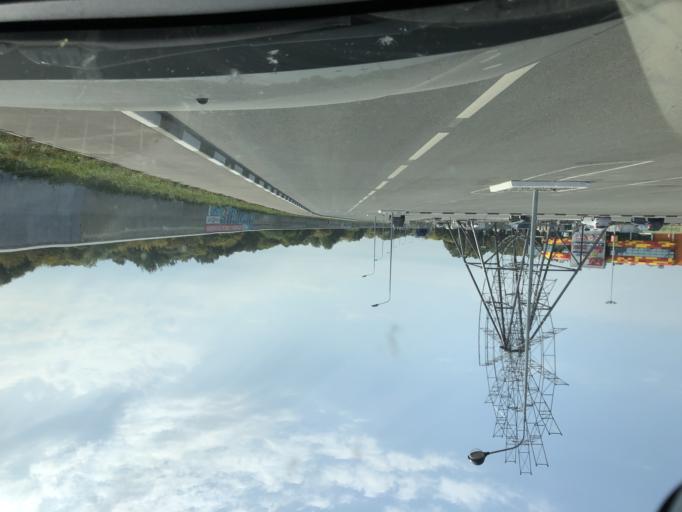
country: RU
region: Tula
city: Tula
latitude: 54.1915
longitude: 37.6358
